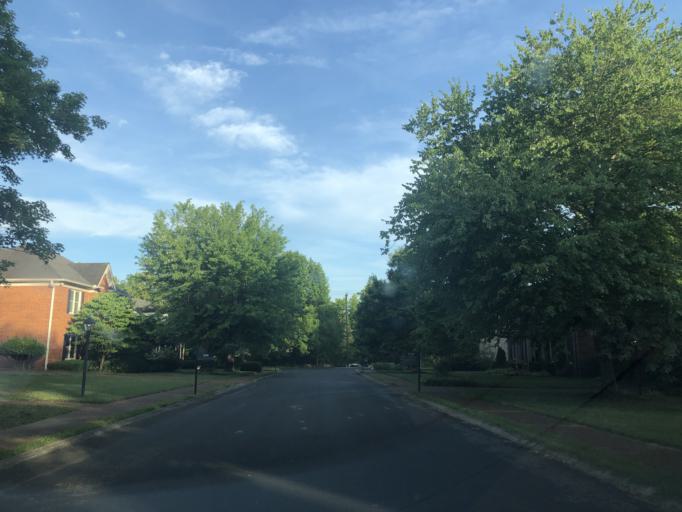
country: US
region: Tennessee
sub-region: Davidson County
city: Belle Meade
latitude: 36.0593
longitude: -86.9221
